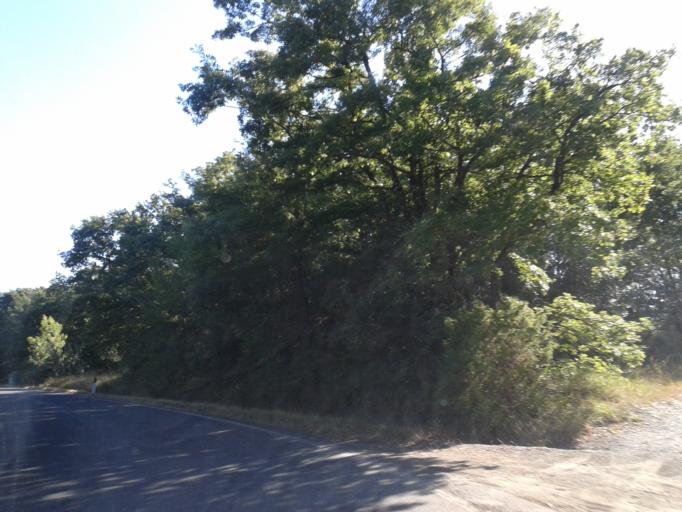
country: IT
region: Tuscany
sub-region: Province of Pisa
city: Castellina Marittima
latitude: 43.4319
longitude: 10.6090
